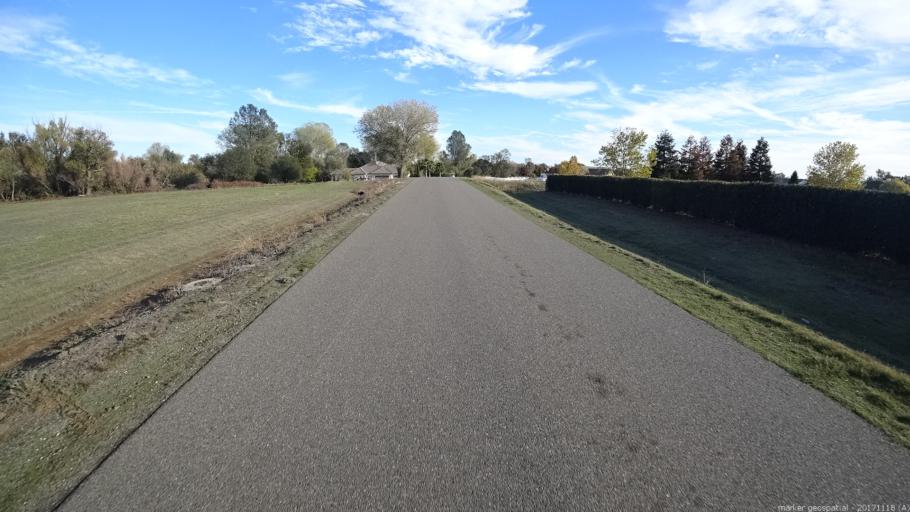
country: US
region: California
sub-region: Shasta County
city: Cottonwood
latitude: 40.3779
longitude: -122.3343
